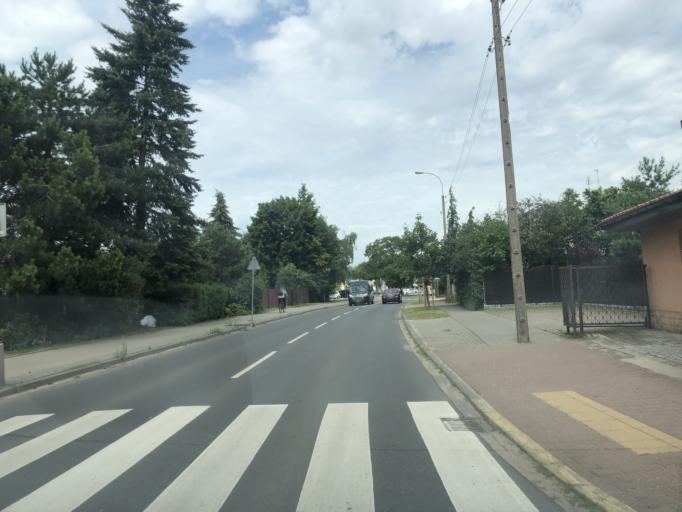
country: PL
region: Greater Poland Voivodeship
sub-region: Powiat poznanski
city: Lubon
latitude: 52.3583
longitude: 16.8821
